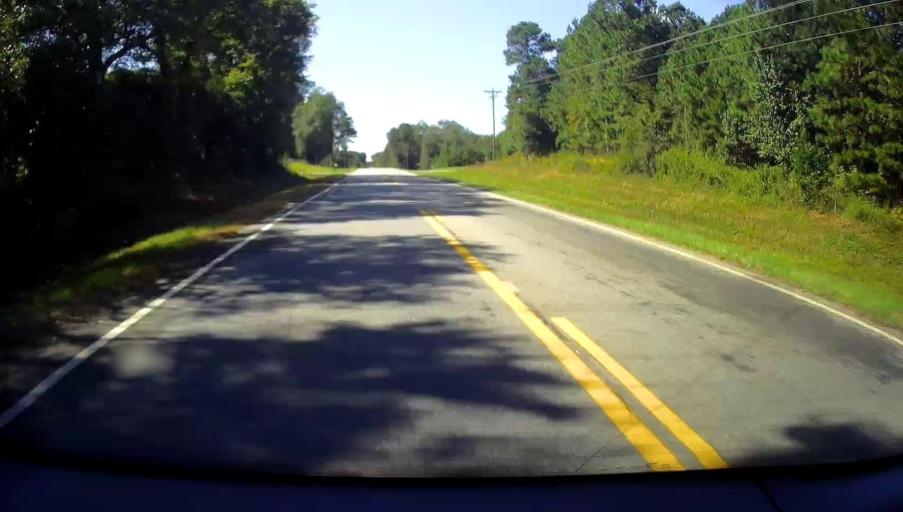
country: US
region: Georgia
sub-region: Jones County
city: Gray
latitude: 32.9444
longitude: -83.4758
